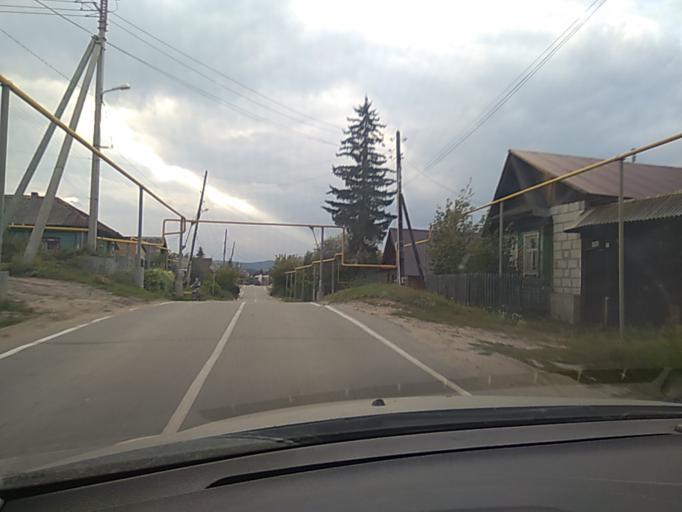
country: RU
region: Chelyabinsk
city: Kyshtym
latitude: 55.6994
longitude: 60.5343
